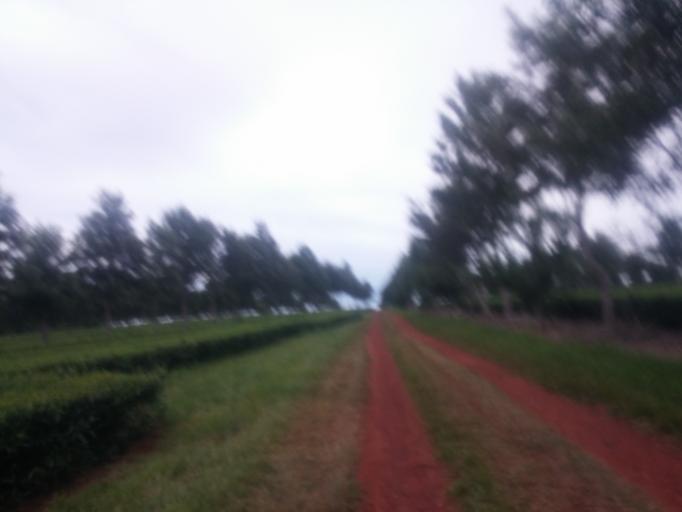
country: AR
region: Misiones
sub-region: Departamento de Obera
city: Obera
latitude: -27.4440
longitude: -55.0875
